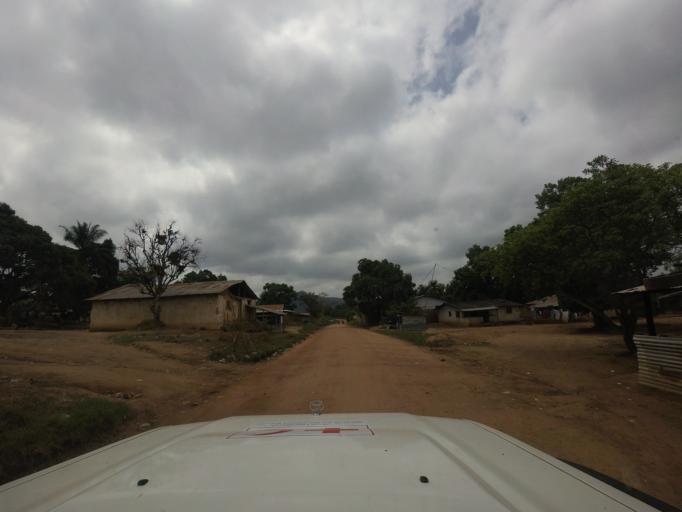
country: LR
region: Lofa
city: Voinjama
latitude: 8.4191
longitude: -9.7465
